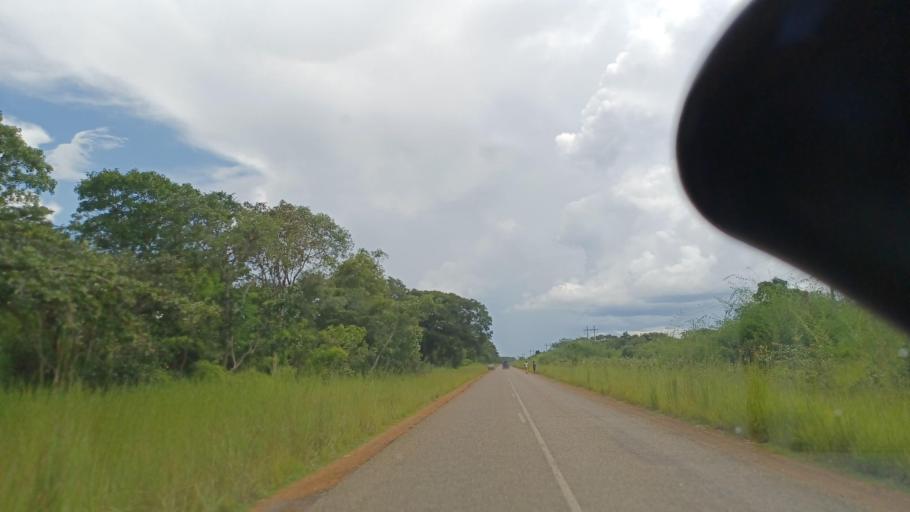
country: ZM
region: North-Western
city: Kasempa
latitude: -13.1338
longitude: 25.8770
